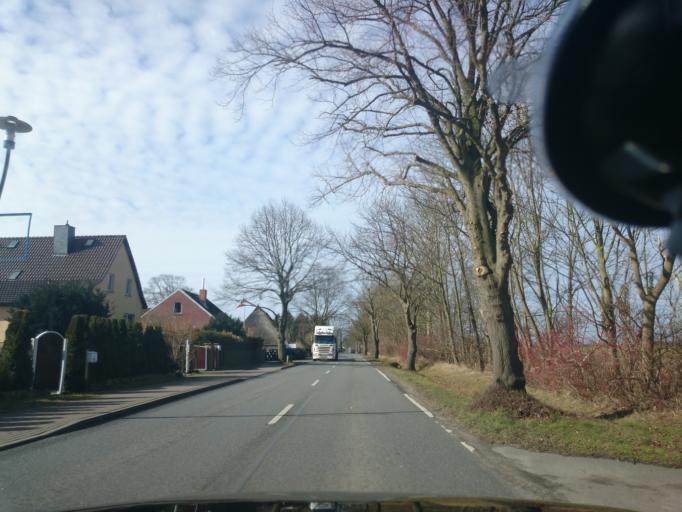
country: DE
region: Mecklenburg-Vorpommern
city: Elmenhorst
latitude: 54.1596
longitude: 11.9944
